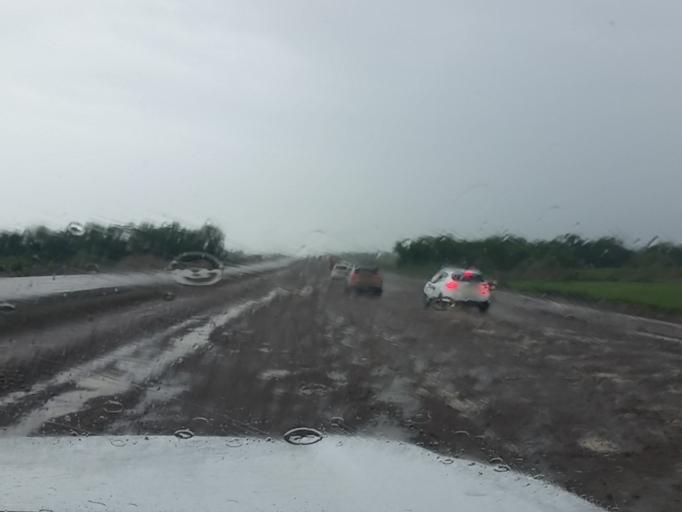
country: KZ
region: Almaty Oblysy
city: Turgen'
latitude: 43.5169
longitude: 77.5063
